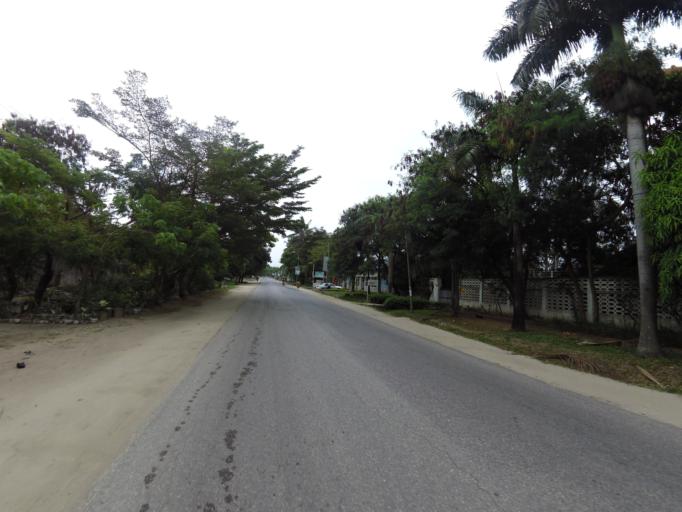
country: TZ
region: Dar es Salaam
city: Magomeni
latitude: -6.7711
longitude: 39.2463
